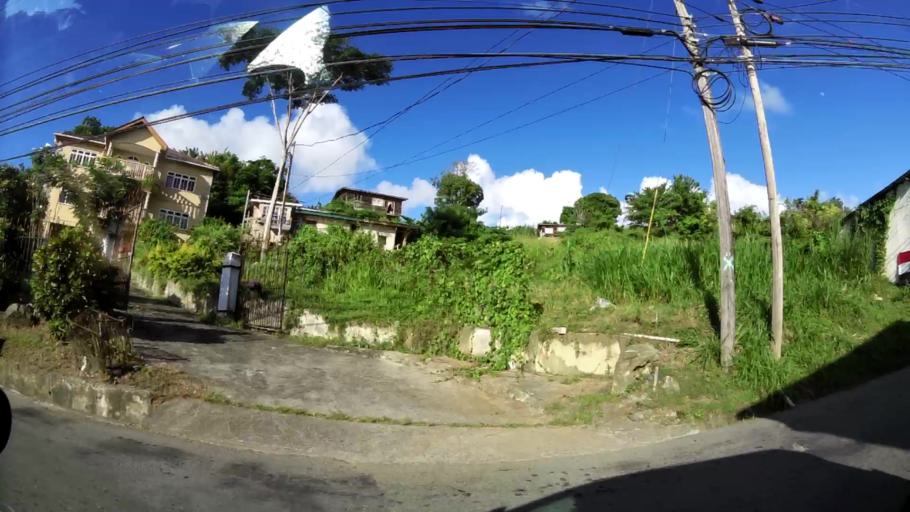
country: TT
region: Tobago
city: Scarborough
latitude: 11.1934
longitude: -60.6860
